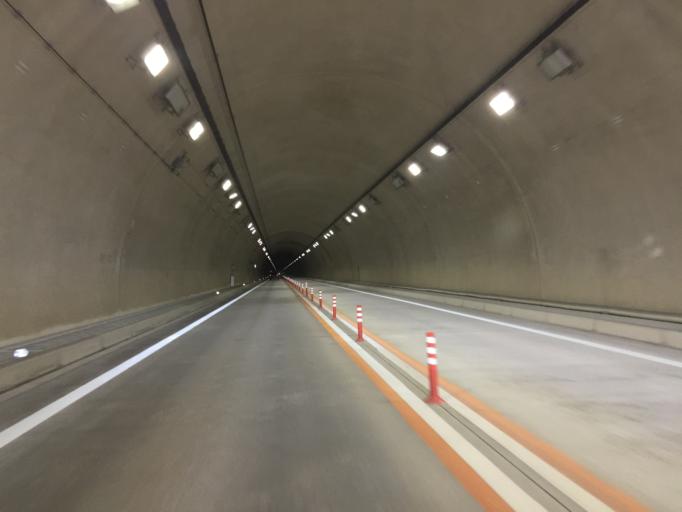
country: JP
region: Fukushima
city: Fukushima-shi
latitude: 37.8092
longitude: 140.4066
